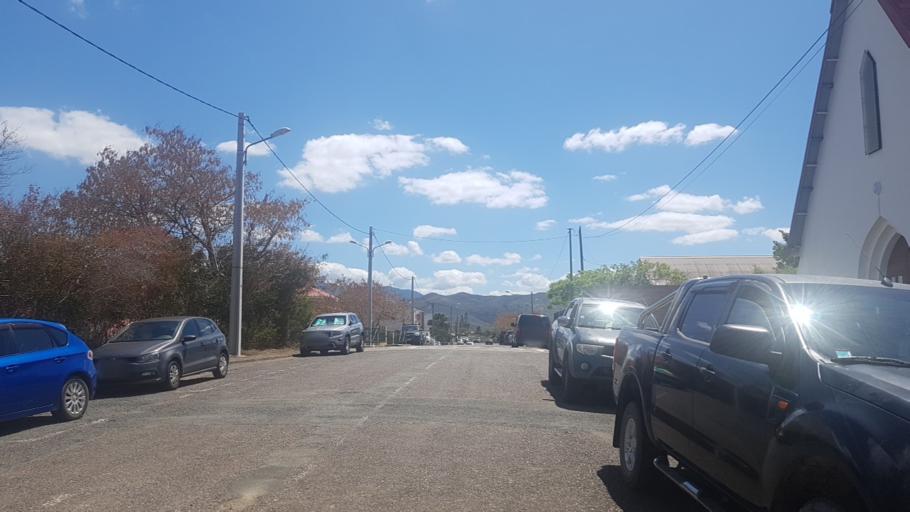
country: NC
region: North Province
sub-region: Kone
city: Kone
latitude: -21.0623
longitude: 164.8610
